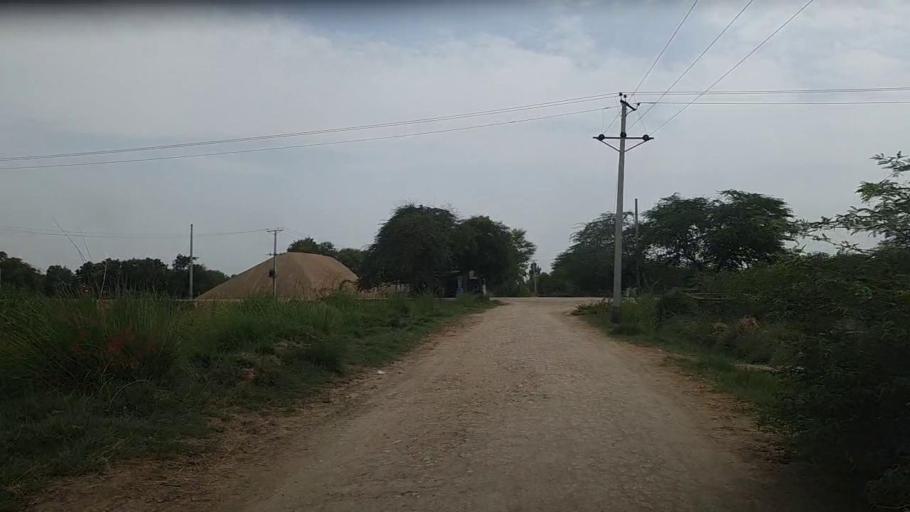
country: PK
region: Sindh
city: Bhiria
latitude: 26.8838
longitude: 68.2954
